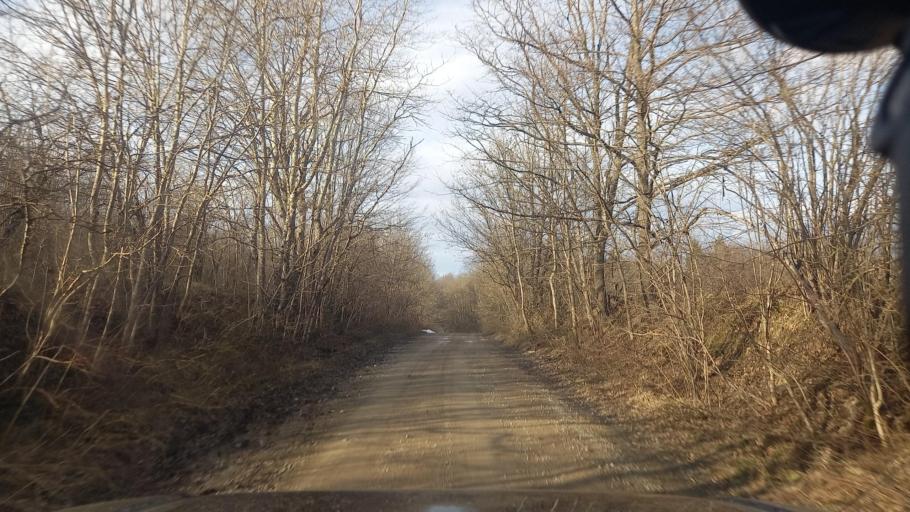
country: RU
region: Krasnodarskiy
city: Goryachiy Klyuch
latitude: 44.6952
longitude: 38.9753
